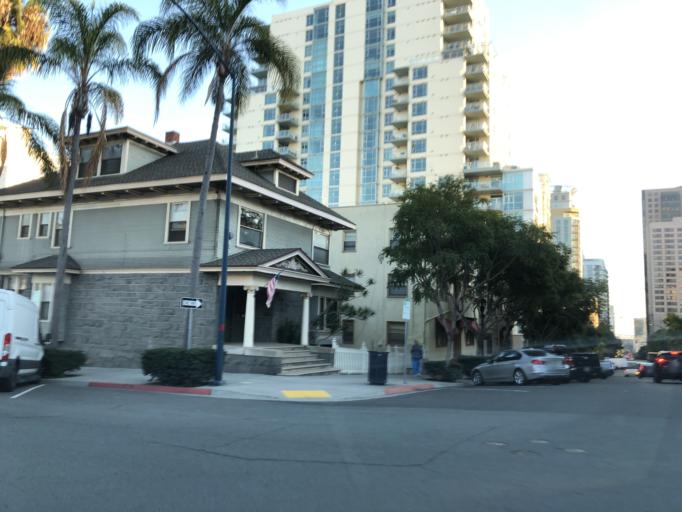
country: US
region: California
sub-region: San Diego County
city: San Diego
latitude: 32.7221
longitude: -117.1575
